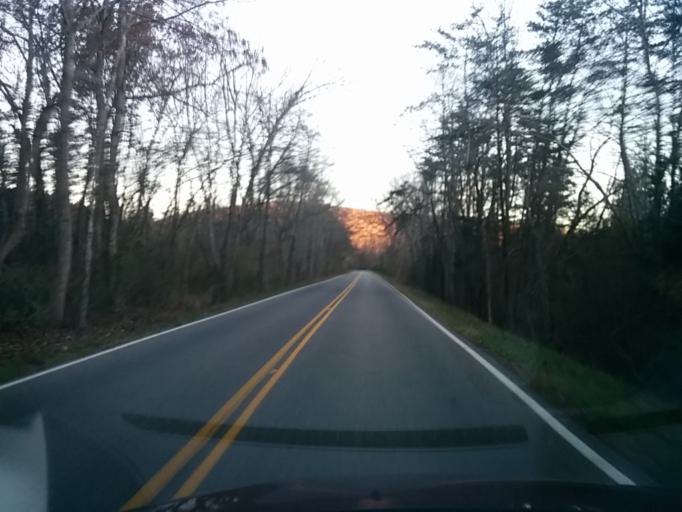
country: US
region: Virginia
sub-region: Rockbridge County
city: East Lexington
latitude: 37.9523
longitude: -79.4660
